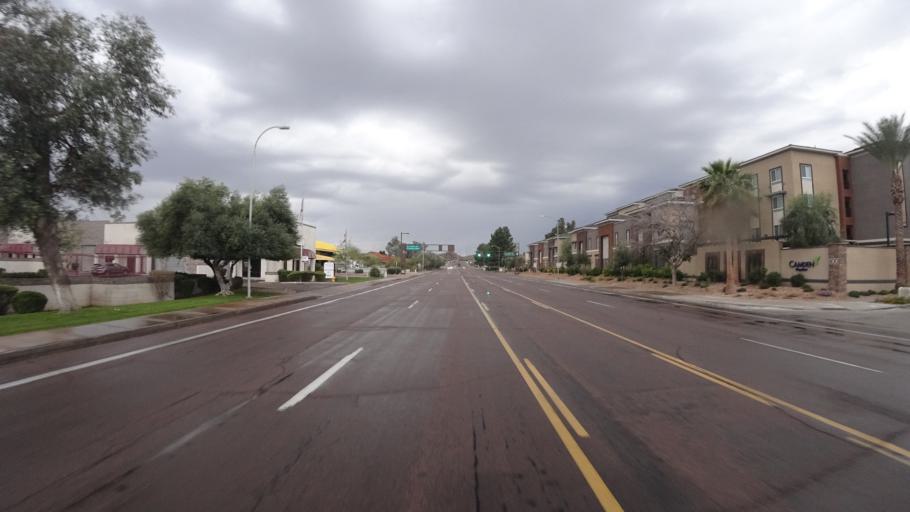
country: US
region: Arizona
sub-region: Maricopa County
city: Tempe Junction
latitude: 33.4402
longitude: -111.9274
